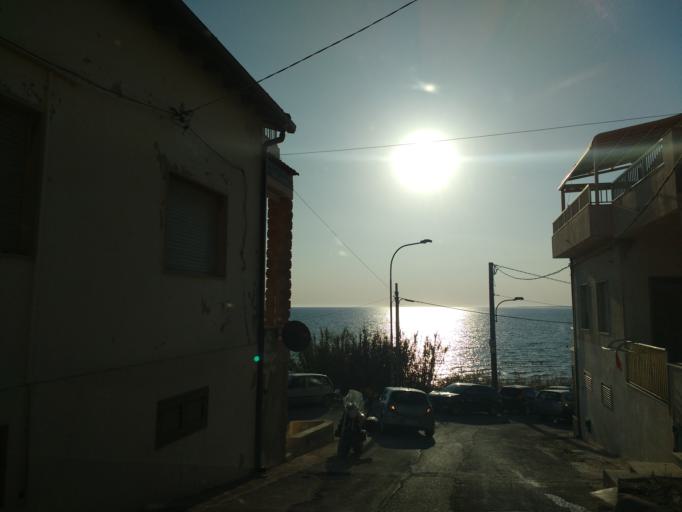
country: IT
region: Sicily
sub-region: Ragusa
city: Cava d'Aliga
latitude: 36.7319
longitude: 14.6816
